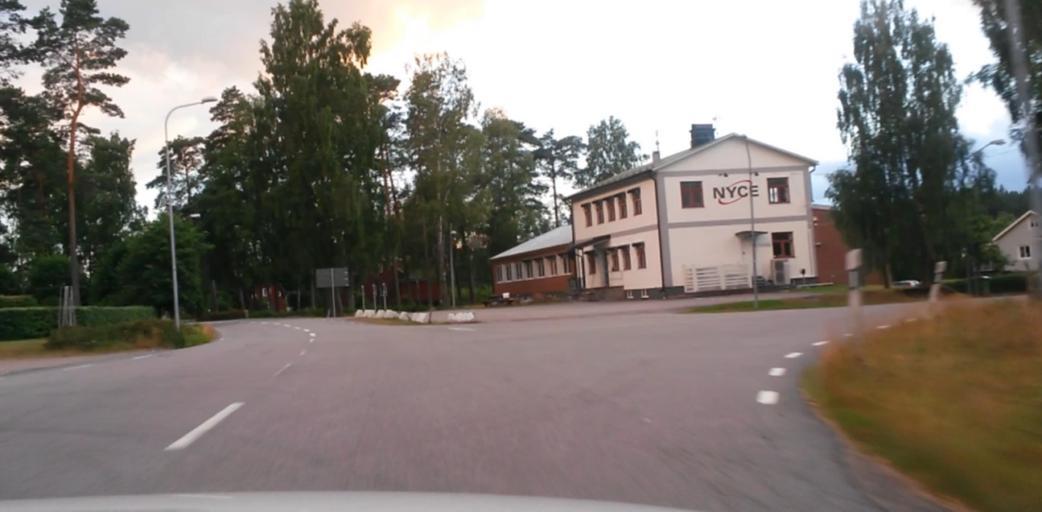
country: SE
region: Vaestra Goetaland
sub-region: Tranemo Kommun
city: Limmared
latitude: 57.5474
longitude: 13.4888
